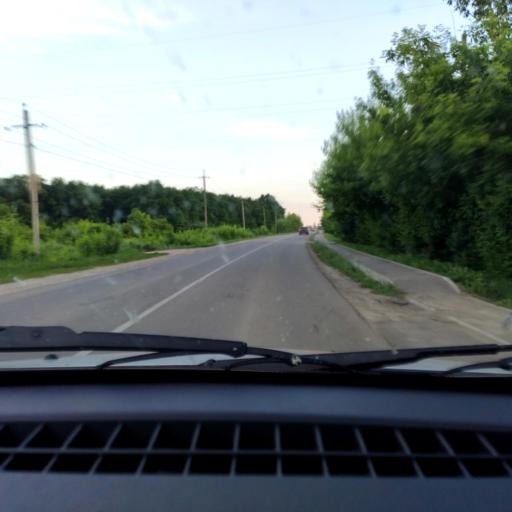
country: RU
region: Voronezj
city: Ramon'
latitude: 51.9501
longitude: 39.3566
